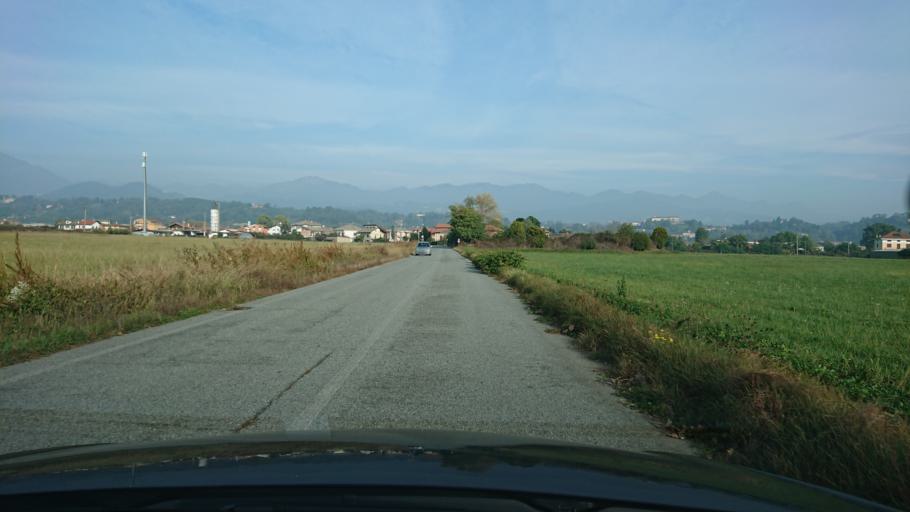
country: IT
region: Piedmont
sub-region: Provincia di Biella
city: Valdengo
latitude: 45.5568
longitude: 8.1333
